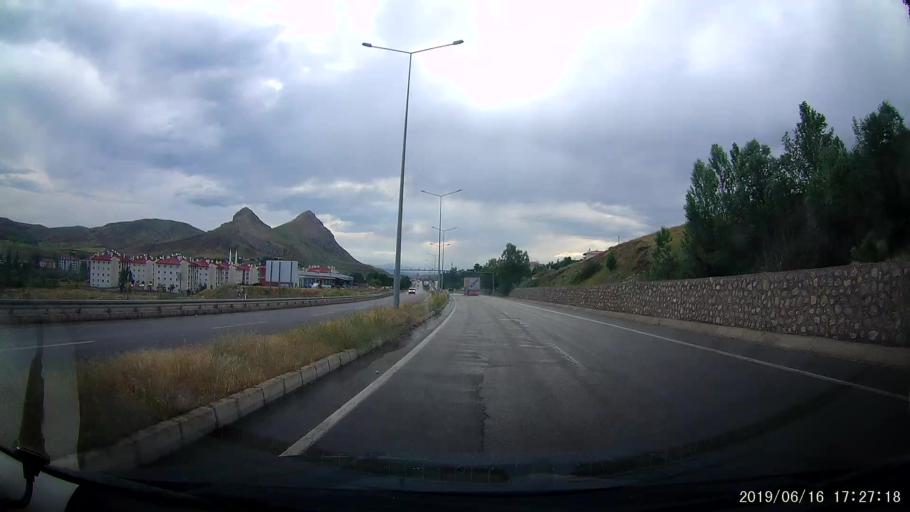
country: TR
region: Erzincan
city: Tercan
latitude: 39.7758
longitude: 40.3957
